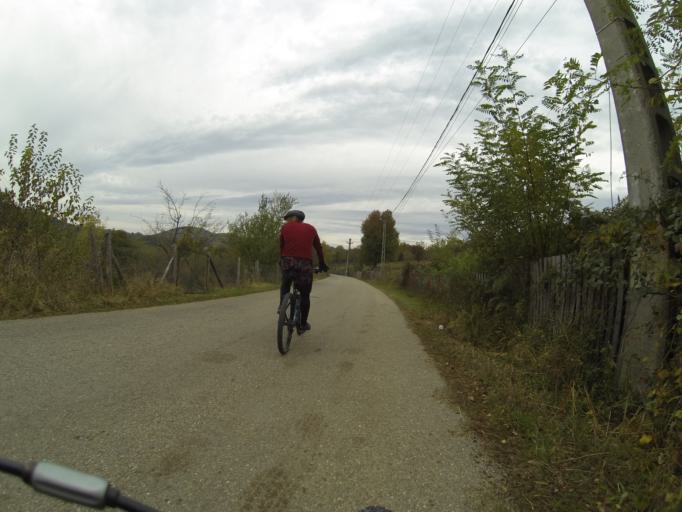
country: RO
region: Gorj
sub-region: Comuna Tismana
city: Sohodol
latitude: 45.0431
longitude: 22.9012
